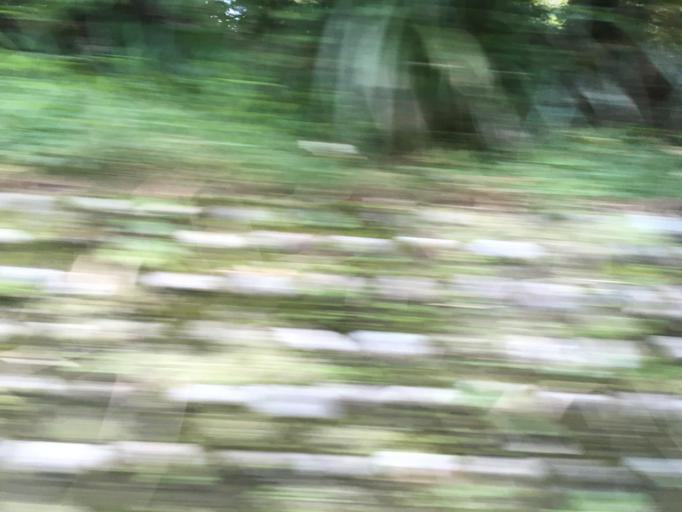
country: TW
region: Taiwan
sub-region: Yilan
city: Yilan
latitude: 24.9309
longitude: 121.6918
